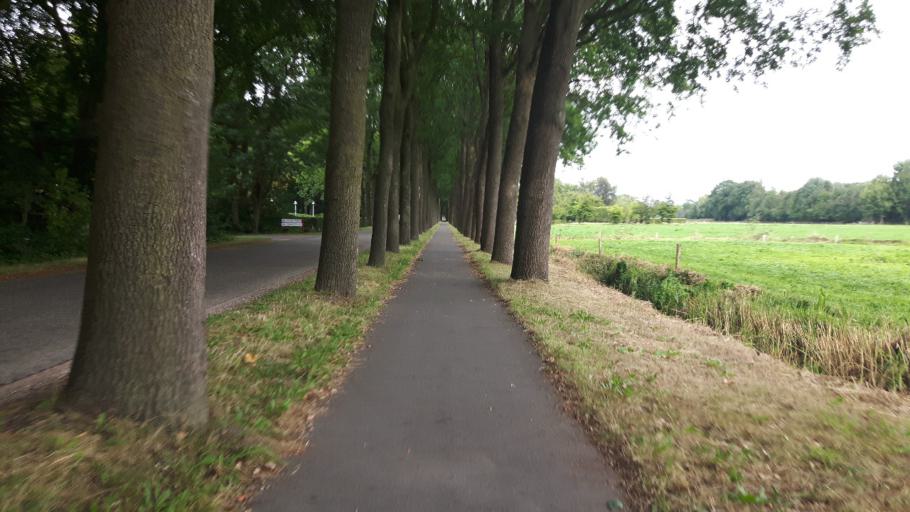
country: NL
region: Gelderland
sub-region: Gemeente Ermelo
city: Horst
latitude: 52.2700
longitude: 5.5655
